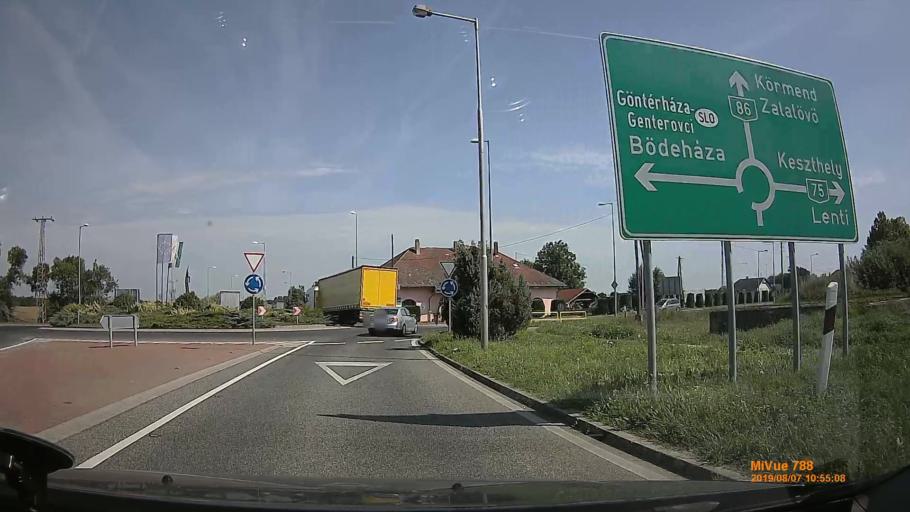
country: SI
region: Lendava-Lendva
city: Lendava
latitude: 46.6172
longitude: 16.4649
